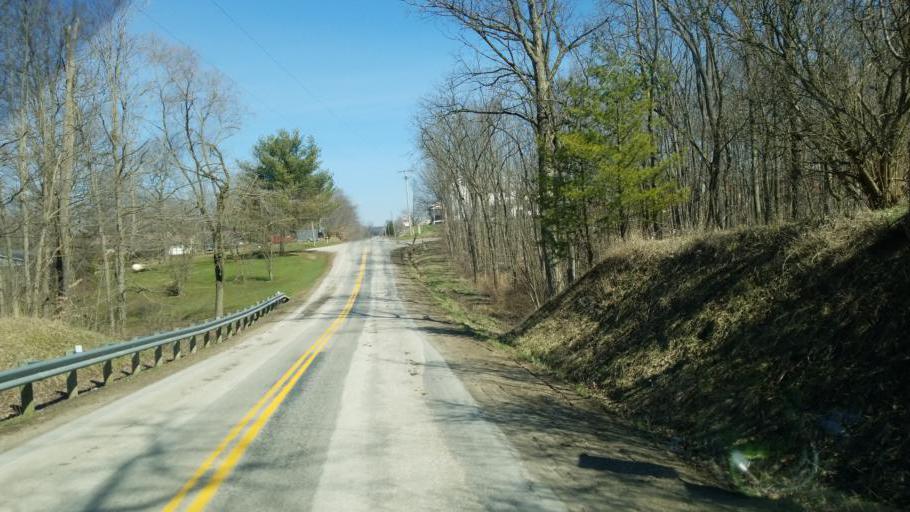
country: US
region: Ohio
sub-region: Ashland County
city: Ashland
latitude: 40.9582
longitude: -82.2438
